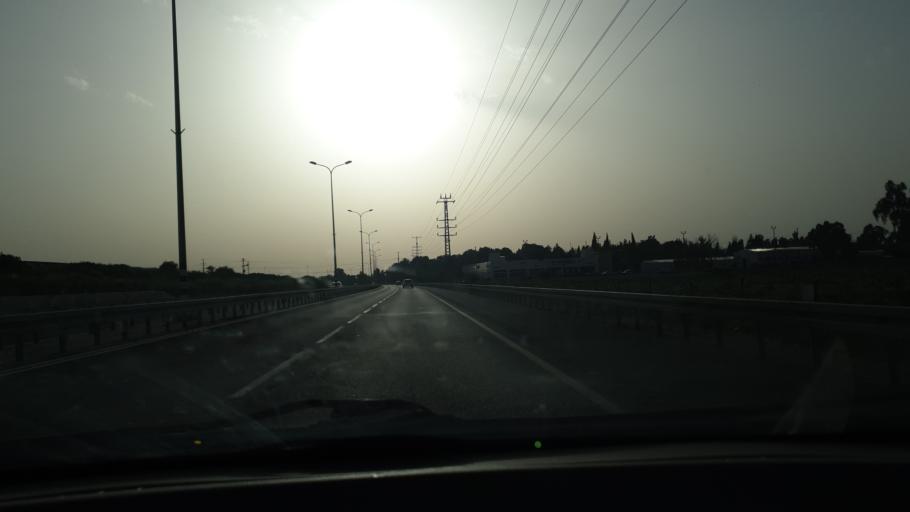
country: IL
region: Central District
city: Tel Mond
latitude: 32.2603
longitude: 34.9077
